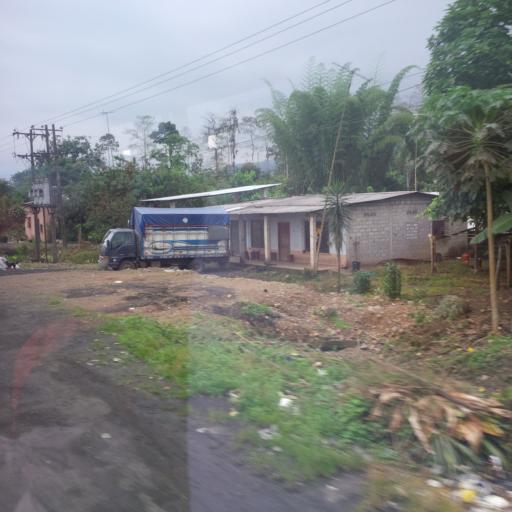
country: EC
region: Canar
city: La Troncal
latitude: -2.2525
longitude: -79.2068
